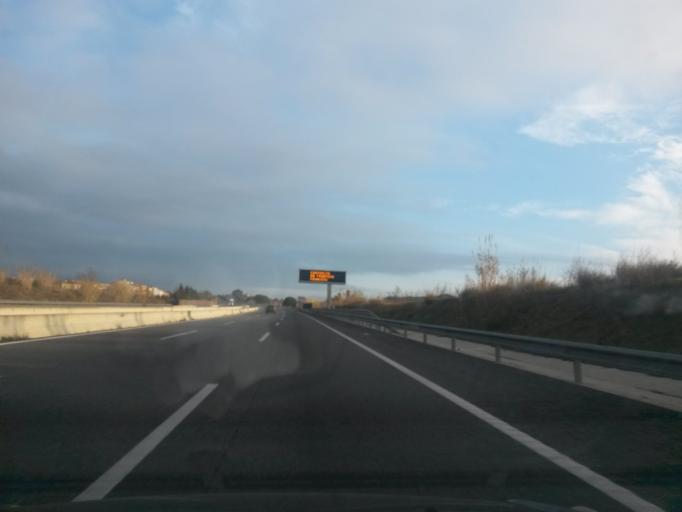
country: ES
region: Catalonia
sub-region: Provincia de Girona
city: Vilafant
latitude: 42.2476
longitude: 2.9416
